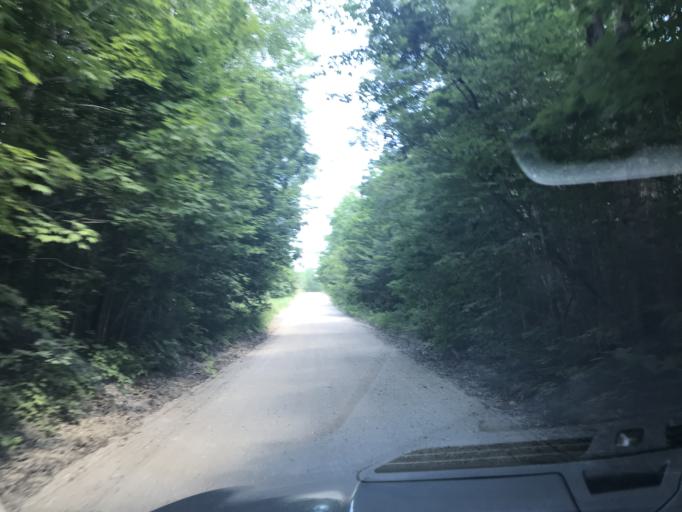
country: US
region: Michigan
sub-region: Cheboygan County
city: Indian River
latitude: 45.5928
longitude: -84.6776
